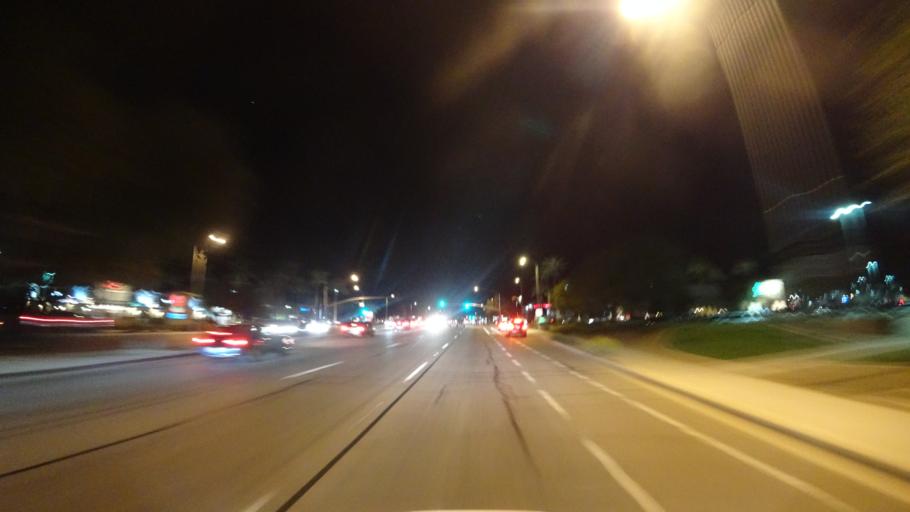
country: US
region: Arizona
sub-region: Maricopa County
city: Chandler
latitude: 33.2808
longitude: -111.7898
